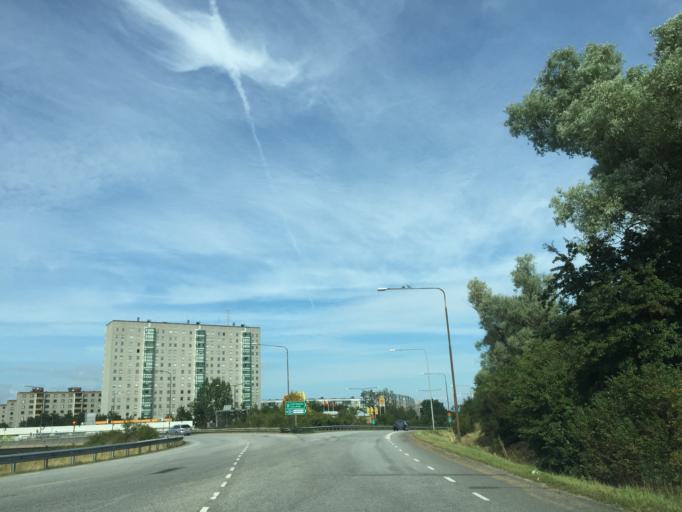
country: SE
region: Skane
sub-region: Burlovs Kommun
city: Arloev
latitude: 55.5822
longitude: 13.0573
